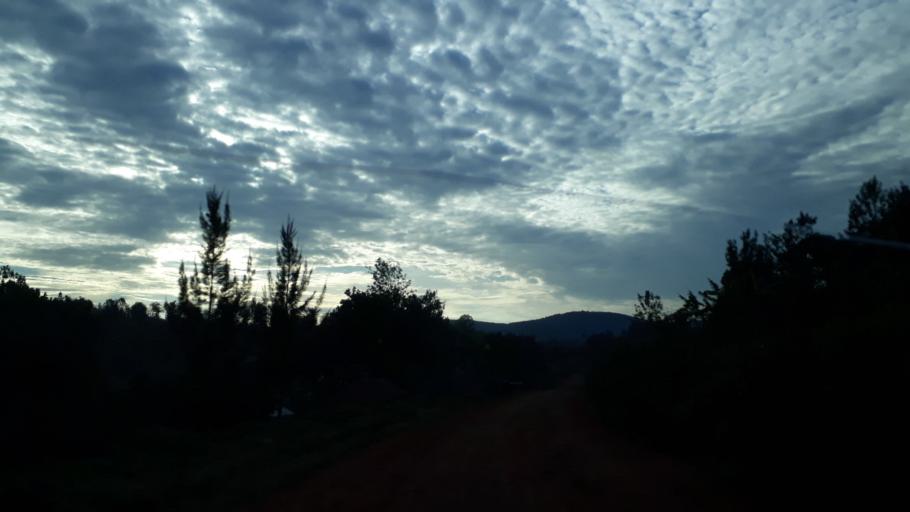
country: UG
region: Northern Region
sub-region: Zombo District
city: Paidha
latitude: 2.2316
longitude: 30.8172
